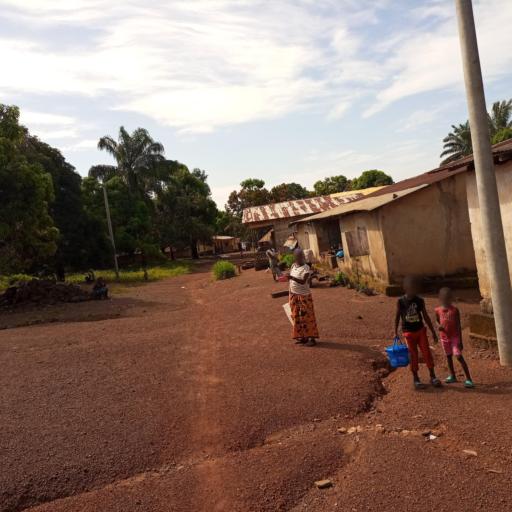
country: SL
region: Northern Province
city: Kambia
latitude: 9.1211
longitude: -12.9148
